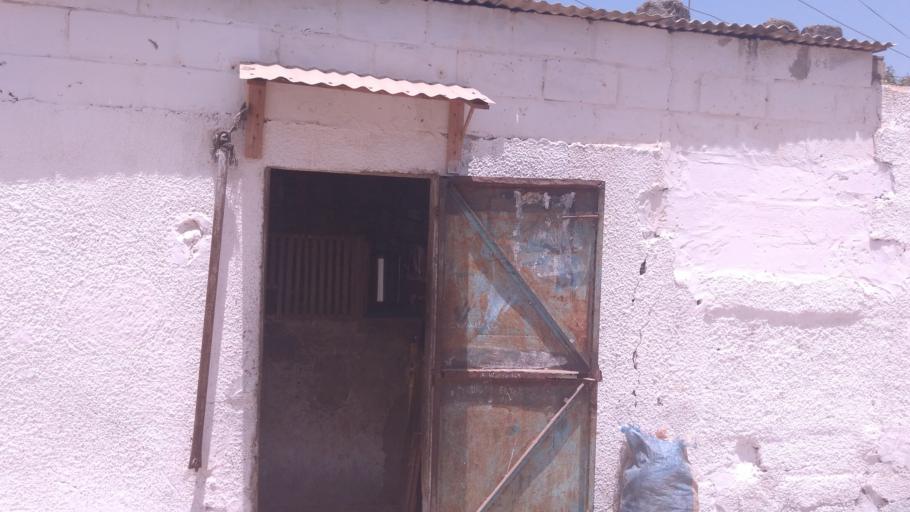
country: SN
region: Dakar
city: Pikine
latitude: 14.6861
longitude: -17.2275
